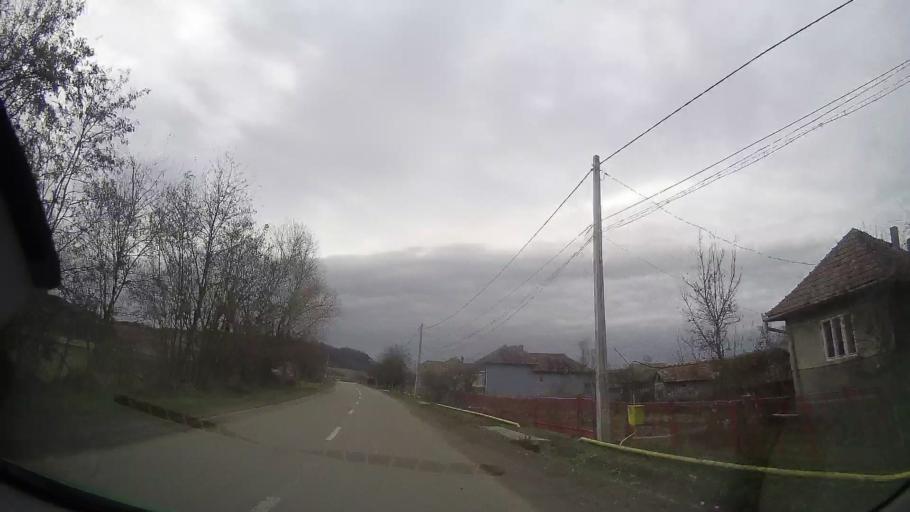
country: RO
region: Bistrita-Nasaud
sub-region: Comuna Milas
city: Milas
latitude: 46.8075
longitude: 24.4277
